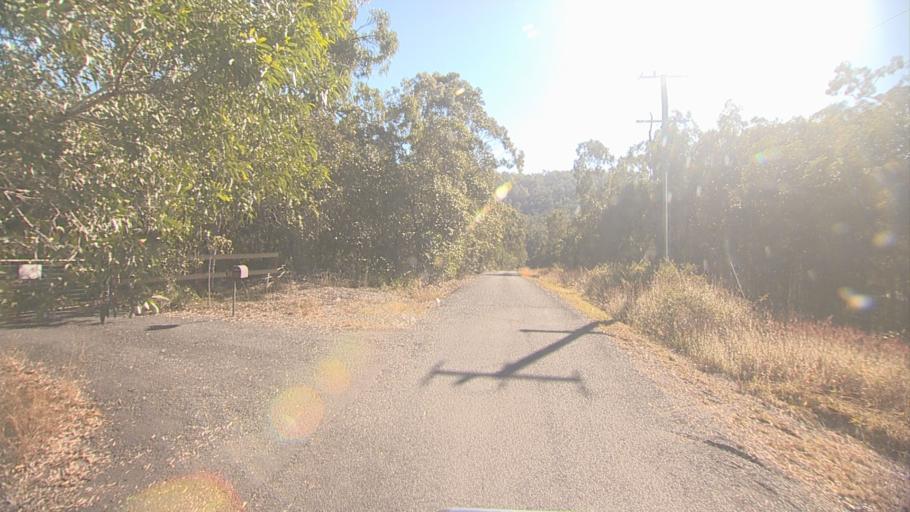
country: AU
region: Queensland
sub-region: Logan
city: Windaroo
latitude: -27.7924
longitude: 153.1707
